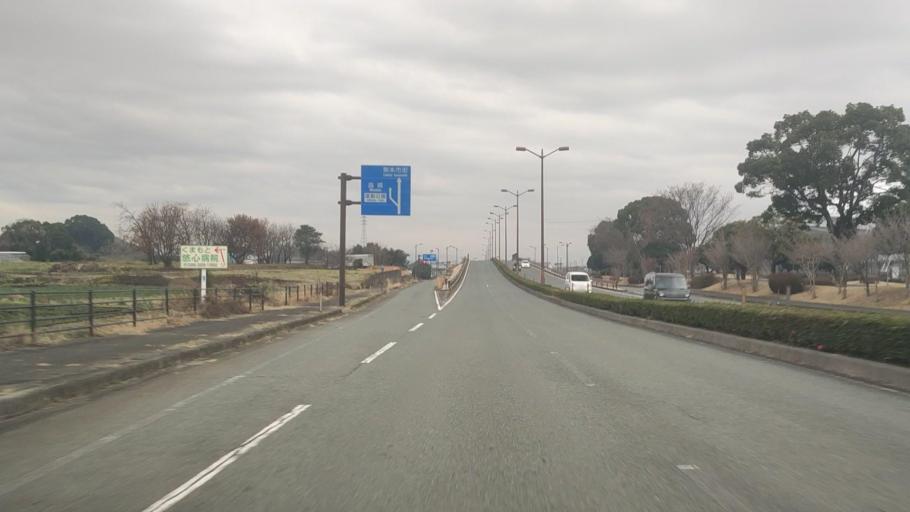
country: JP
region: Kumamoto
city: Ozu
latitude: 32.8381
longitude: 130.8041
